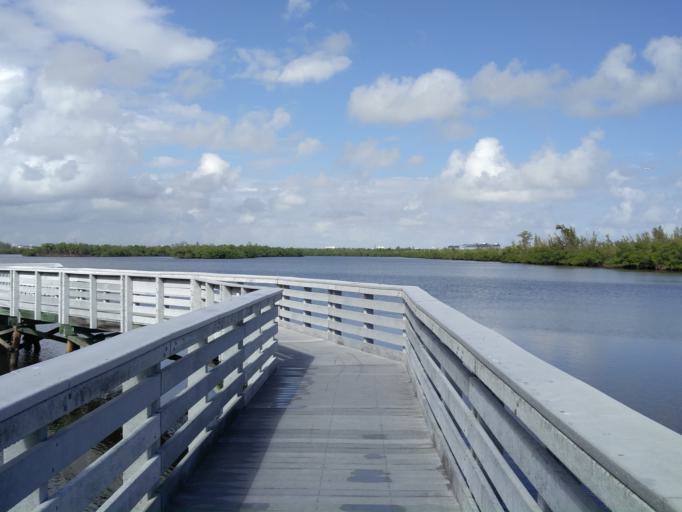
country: US
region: Florida
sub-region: Broward County
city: Dania Beach
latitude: 26.0396
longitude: -80.1215
